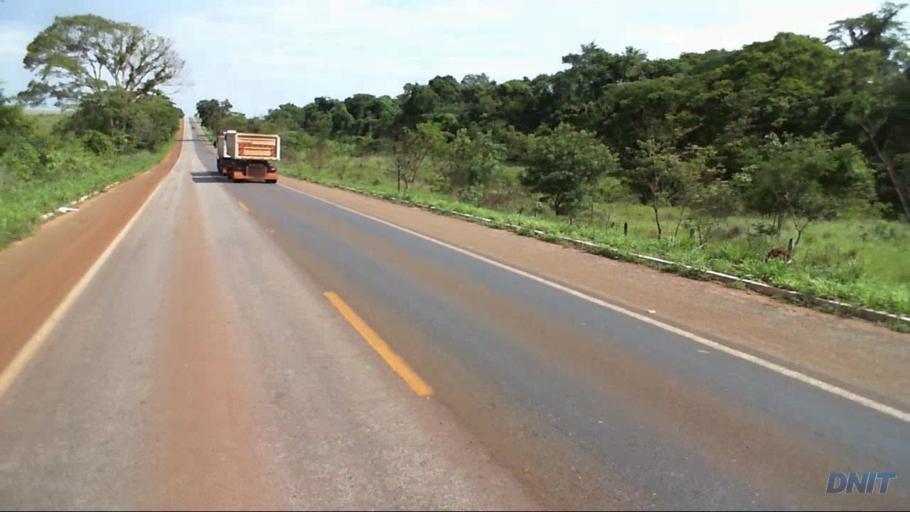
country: BR
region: Goias
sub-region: Barro Alto
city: Barro Alto
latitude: -15.0105
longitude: -48.9012
